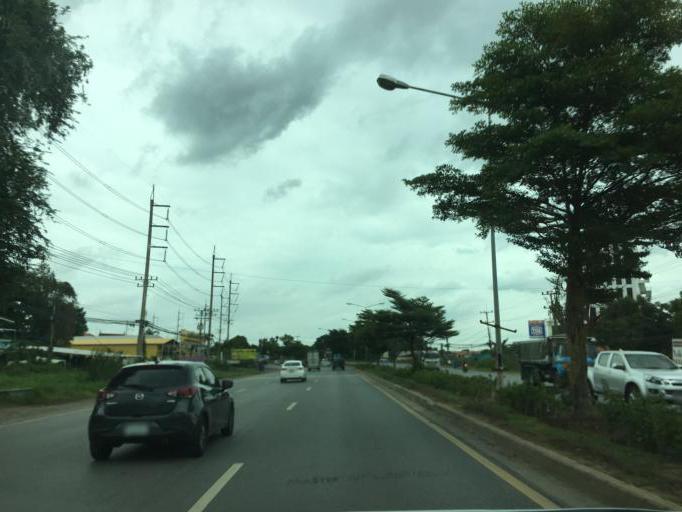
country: TH
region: Phra Nakhon Si Ayutthaya
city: Wang Noi
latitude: 14.2773
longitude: 100.6804
